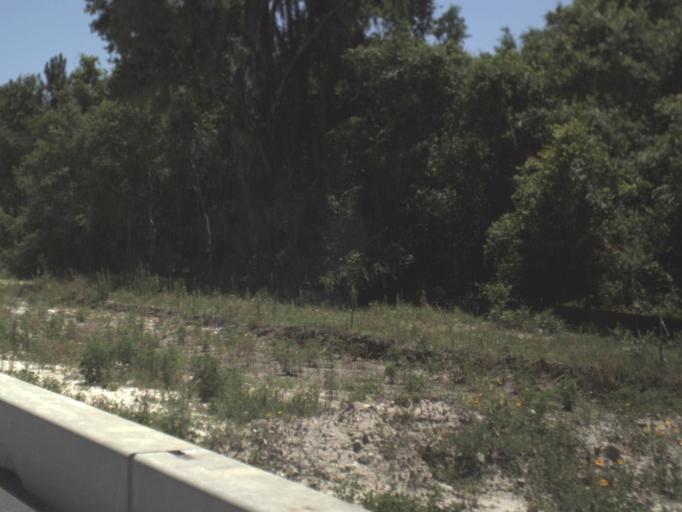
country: US
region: Florida
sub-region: Columbia County
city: Lake City
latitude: 30.1896
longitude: -82.7205
